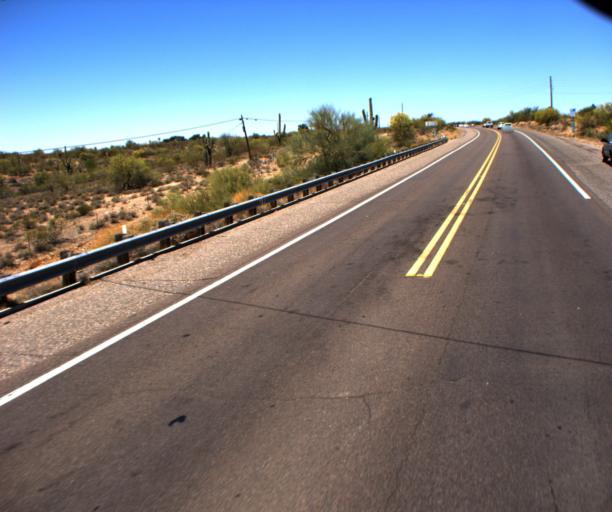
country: US
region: Arizona
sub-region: Maricopa County
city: Wickenburg
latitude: 33.9975
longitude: -112.7579
